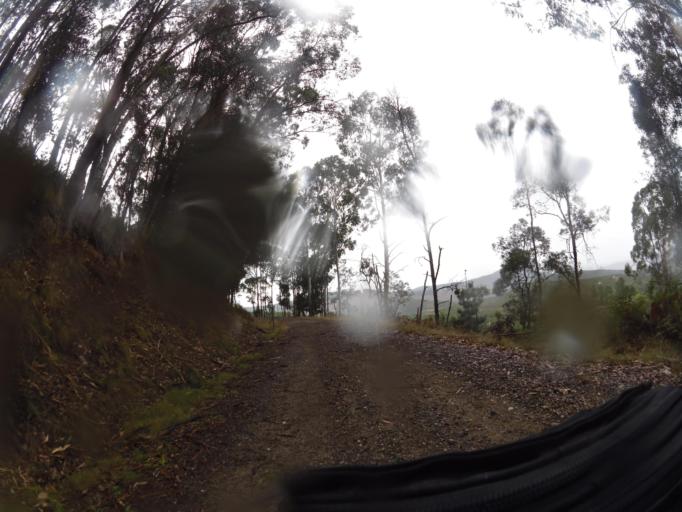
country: AU
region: New South Wales
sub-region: Greater Hume Shire
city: Holbrook
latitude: -36.2197
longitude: 147.5651
